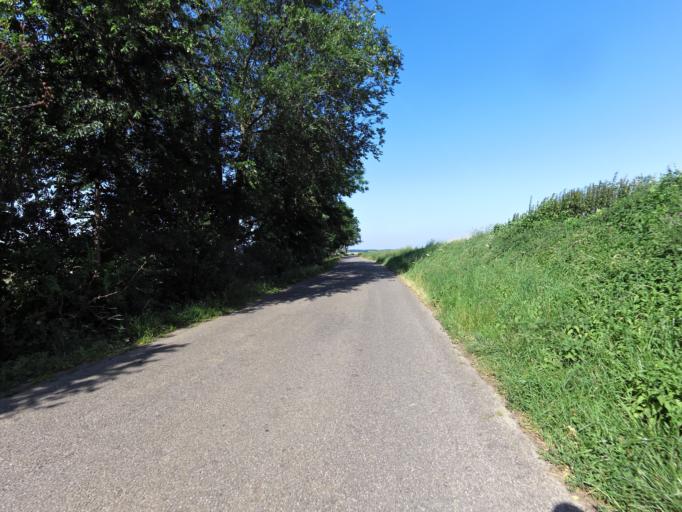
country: NL
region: Limburg
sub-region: Valkenburg aan de Geul
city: Valkenburg
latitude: 50.8689
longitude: 5.8522
